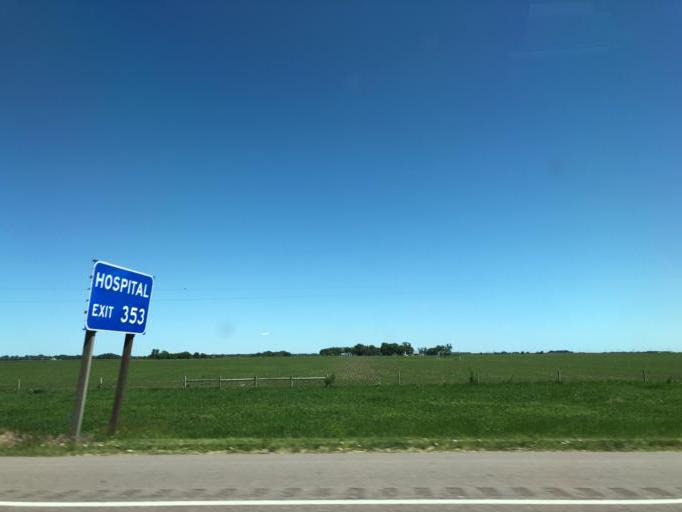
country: US
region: Nebraska
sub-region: York County
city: York
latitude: 40.8223
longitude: -97.5644
